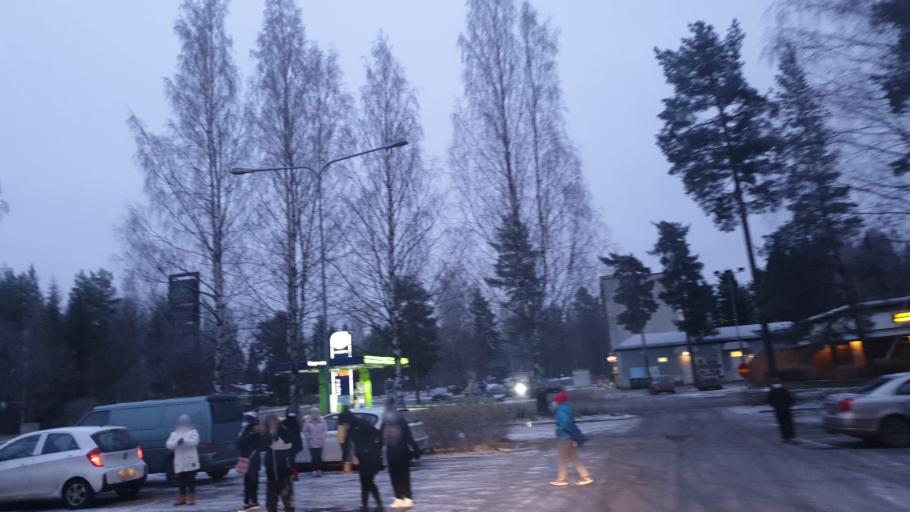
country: FI
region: Southern Ostrobothnia
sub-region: Seinaejoki
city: Seinaejoki
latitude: 62.7712
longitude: 22.8768
